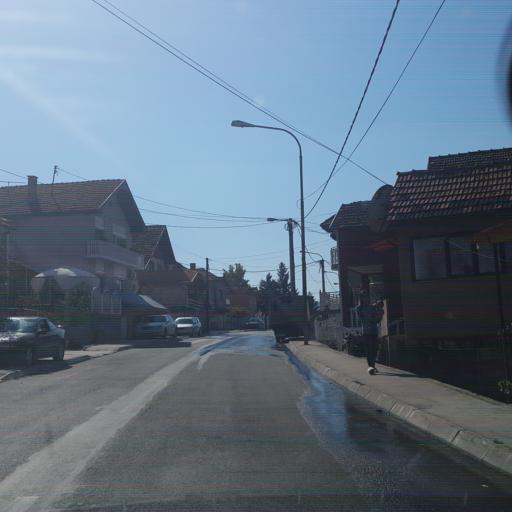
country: RS
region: Central Serbia
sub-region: Zajecarski Okrug
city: Knjazevac
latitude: 43.5584
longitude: 22.2529
